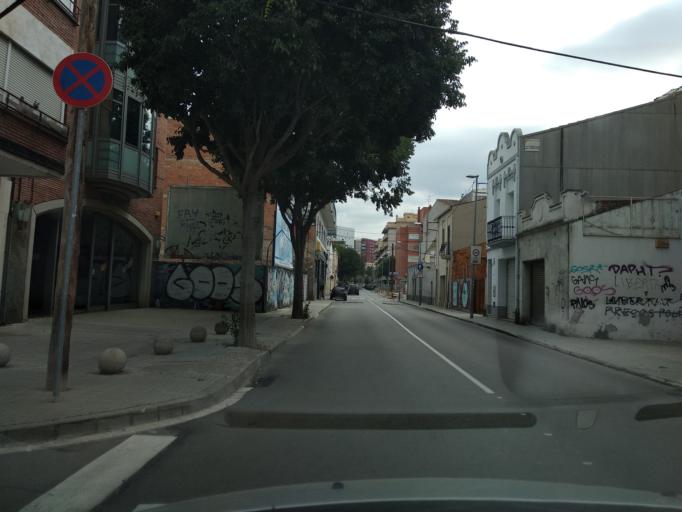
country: ES
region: Catalonia
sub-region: Provincia de Barcelona
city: Granollers
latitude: 41.6031
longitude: 2.2886
